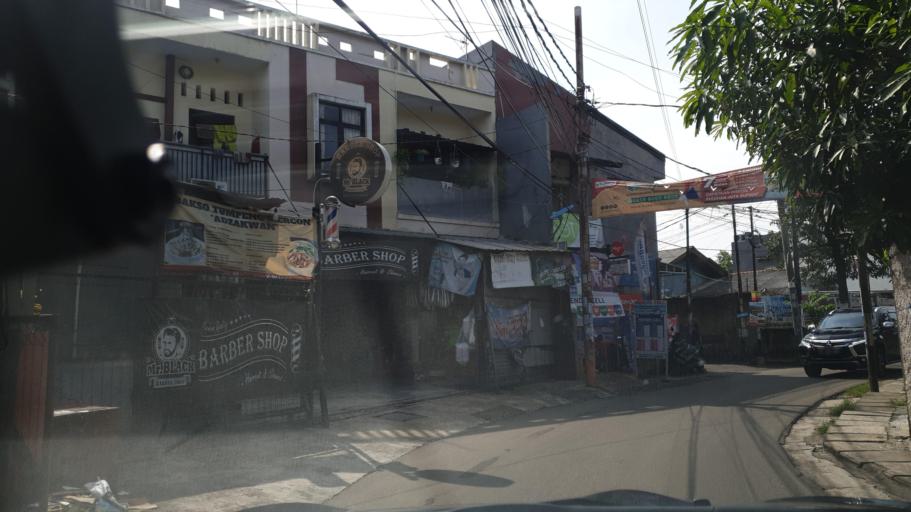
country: ID
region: West Java
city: Pamulang
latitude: -6.3183
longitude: 106.7550
